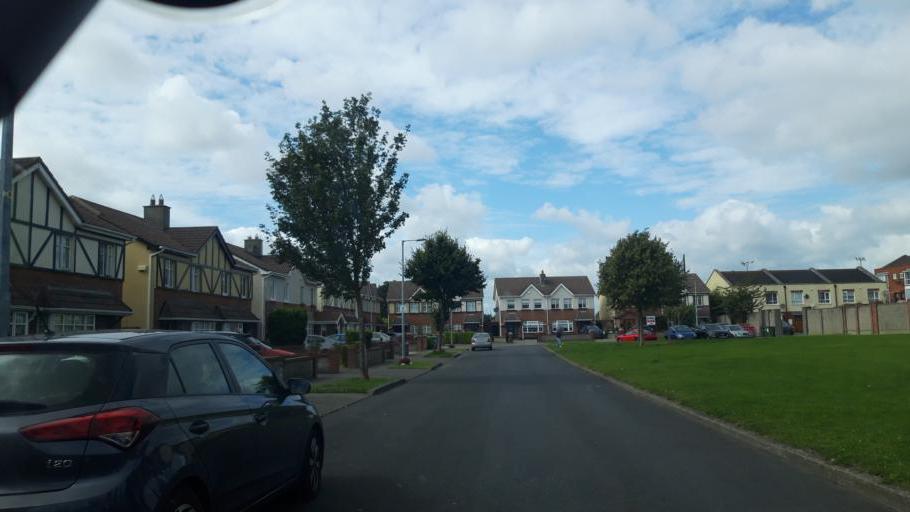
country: IE
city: Darndale
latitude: 53.3979
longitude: -6.1809
